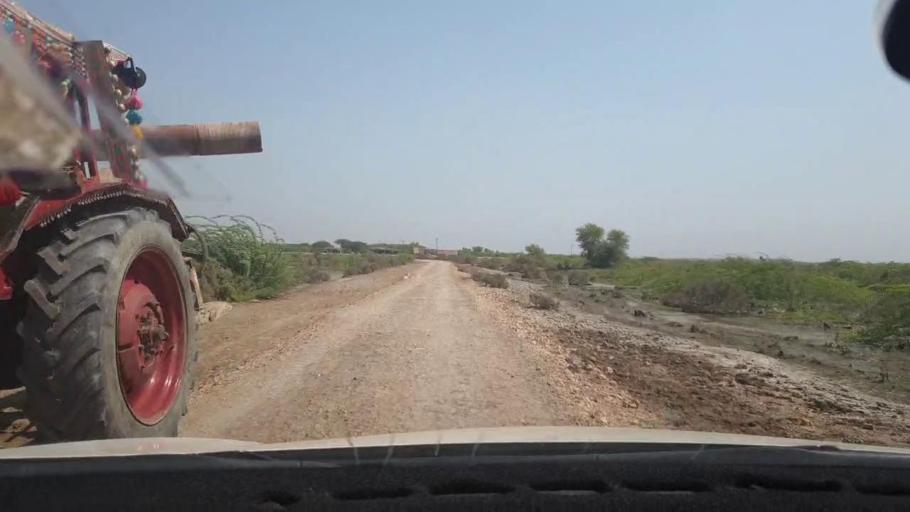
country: PK
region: Sindh
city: Tando Mittha Khan
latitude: 25.9165
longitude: 69.2528
